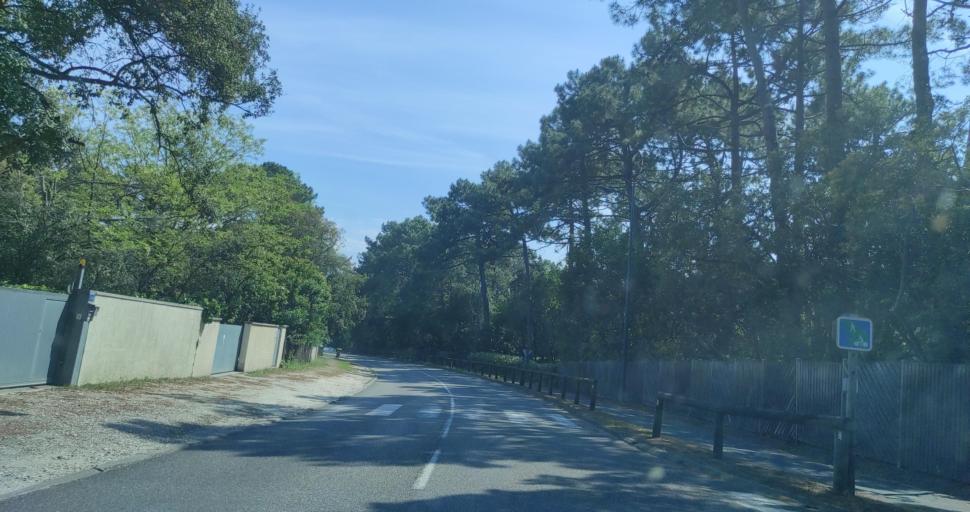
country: FR
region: Aquitaine
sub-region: Departement de la Gironde
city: Arcachon
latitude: 44.6890
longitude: -1.2396
